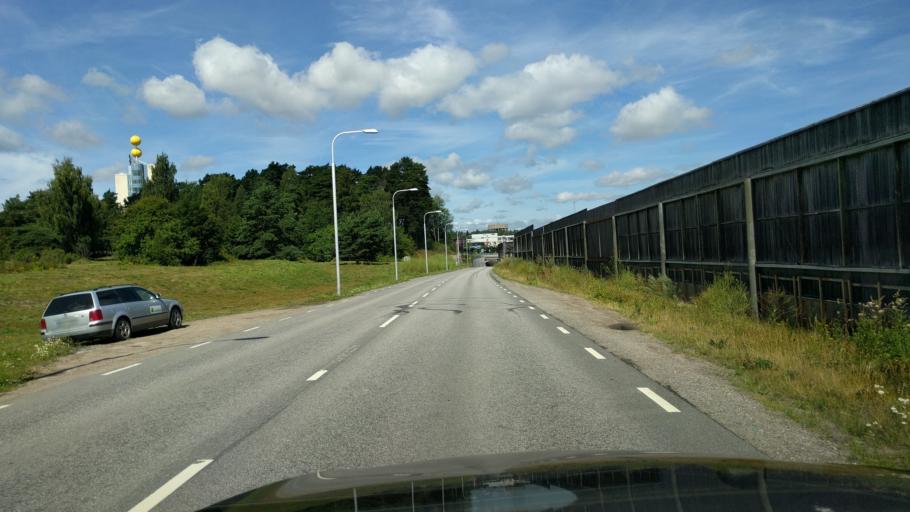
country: SE
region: Stockholm
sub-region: Taby Kommun
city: Taby
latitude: 59.4423
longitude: 18.0769
